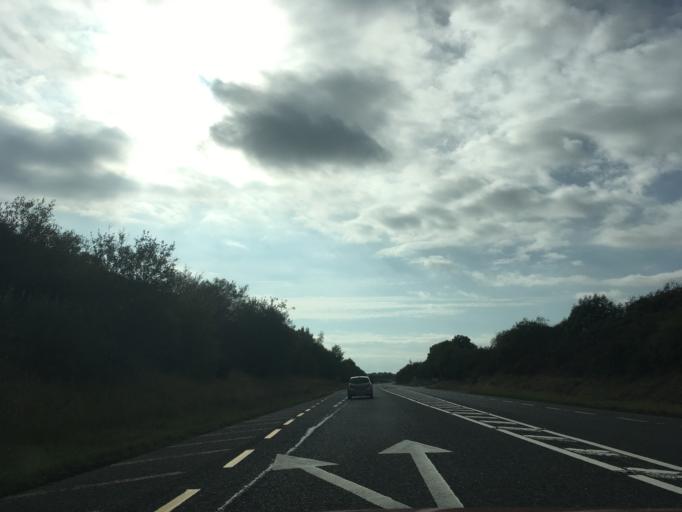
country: IE
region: Leinster
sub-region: Loch Garman
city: Loch Garman
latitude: 52.3478
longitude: -6.6162
